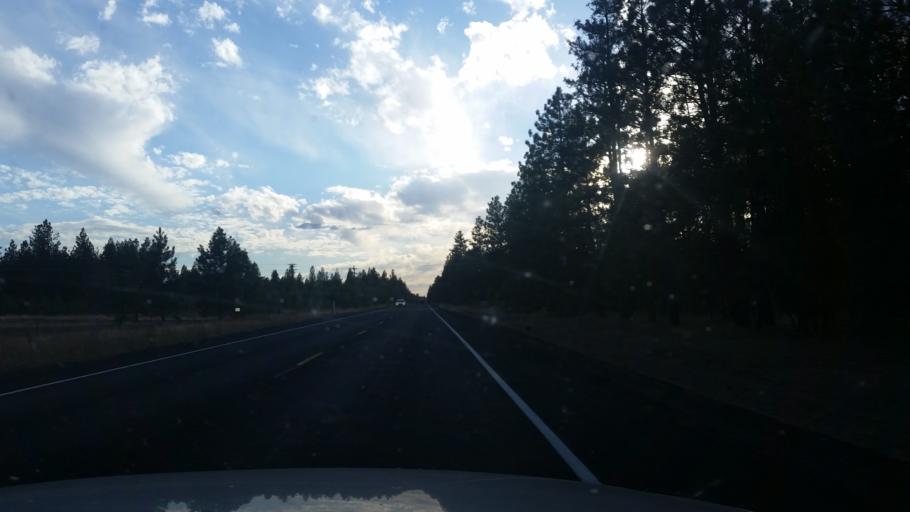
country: US
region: Washington
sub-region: Spokane County
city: Cheney
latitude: 47.4618
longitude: -117.6801
